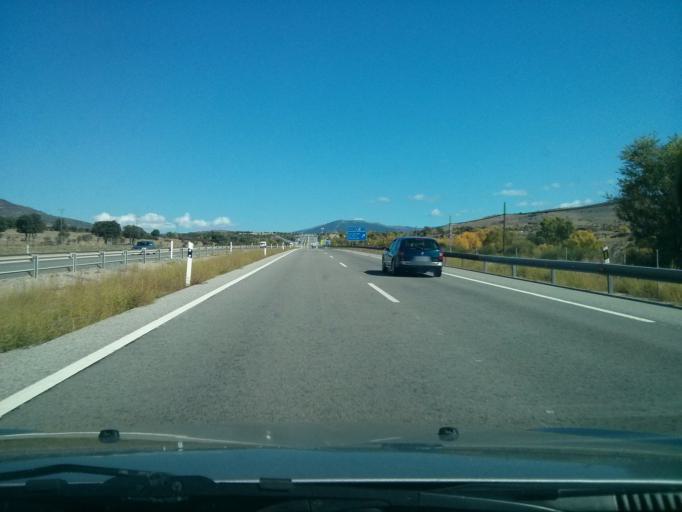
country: ES
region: Madrid
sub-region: Provincia de Madrid
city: Gascones
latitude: 41.0174
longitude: -3.6280
